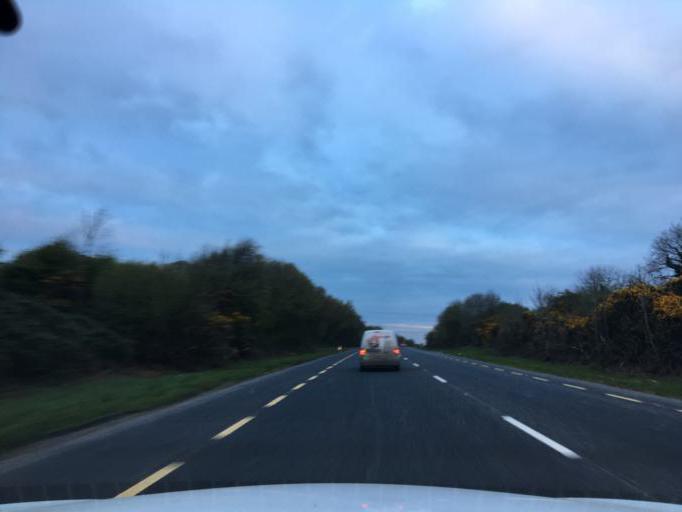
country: IE
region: Leinster
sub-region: Loch Garman
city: Loch Garman
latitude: 52.3148
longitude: -6.4919
